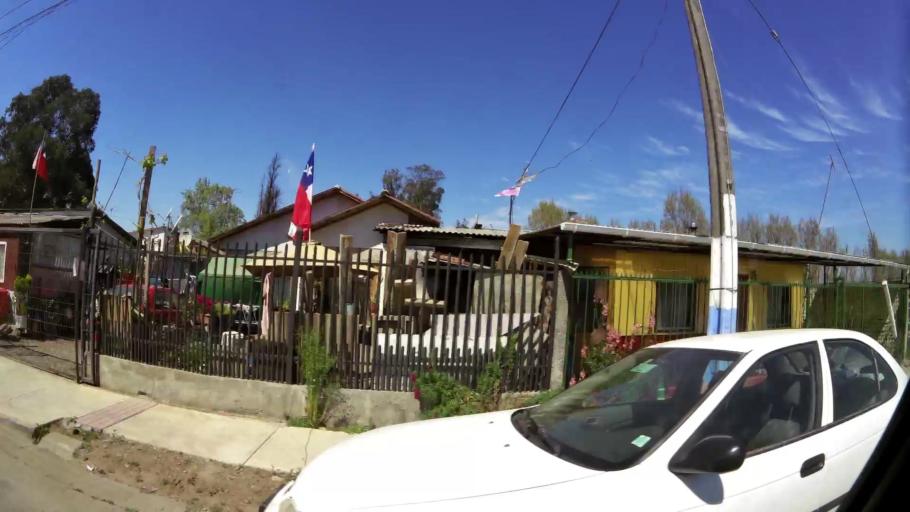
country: CL
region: Santiago Metropolitan
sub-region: Provincia de Talagante
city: Talagante
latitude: -33.6557
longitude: -70.9274
